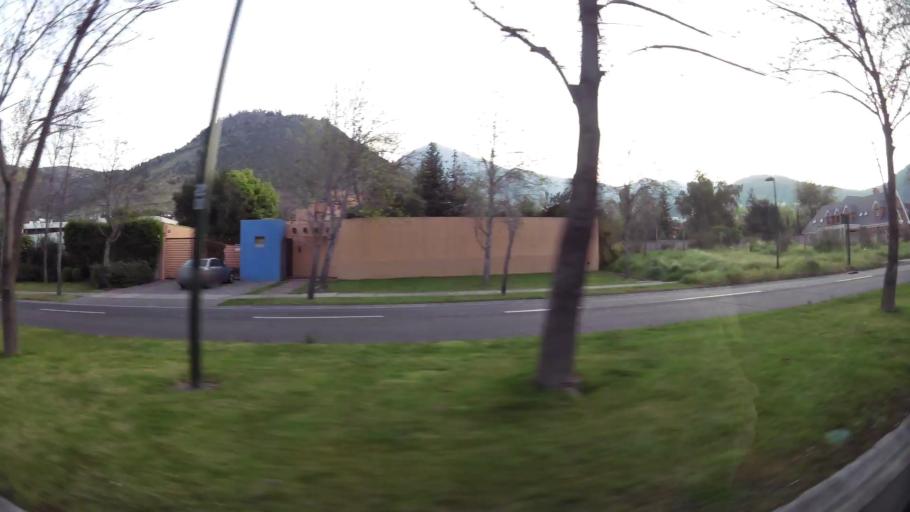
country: CL
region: Santiago Metropolitan
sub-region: Provincia de Chacabuco
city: Chicureo Abajo
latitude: -33.3418
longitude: -70.5537
